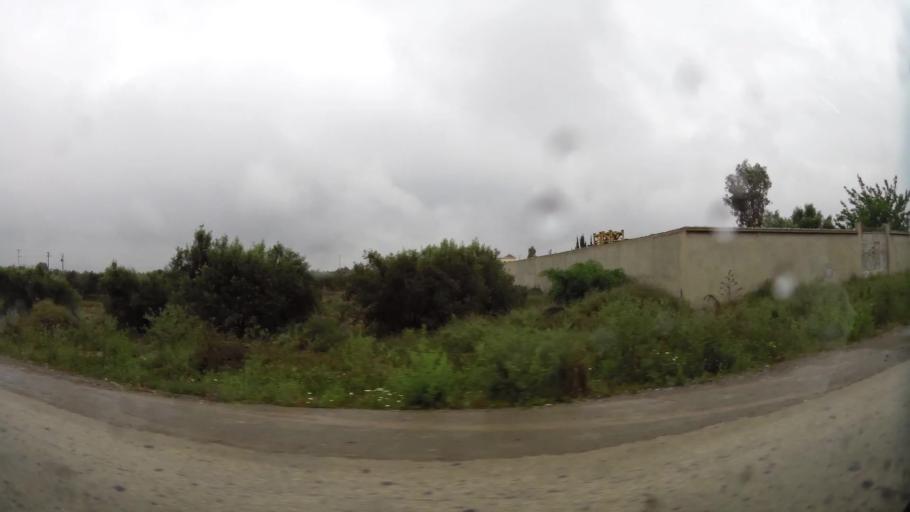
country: MA
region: Taza-Al Hoceima-Taounate
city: Imzourene
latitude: 35.1531
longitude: -3.8204
